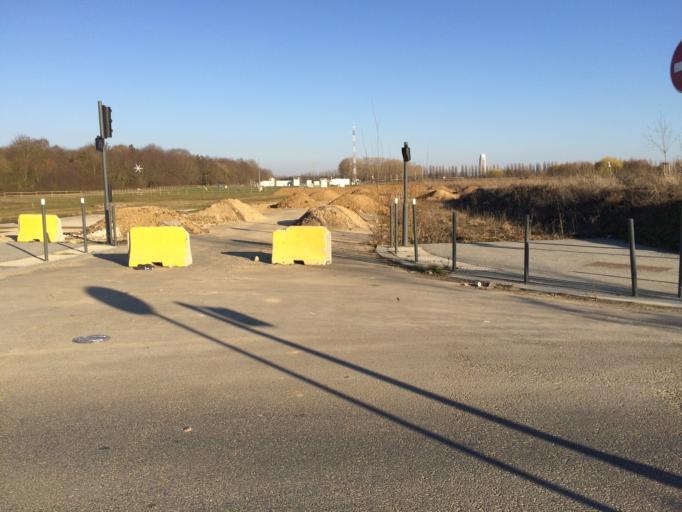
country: FR
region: Ile-de-France
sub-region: Departement de l'Essonne
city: Vauhallan
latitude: 48.7181
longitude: 2.2031
